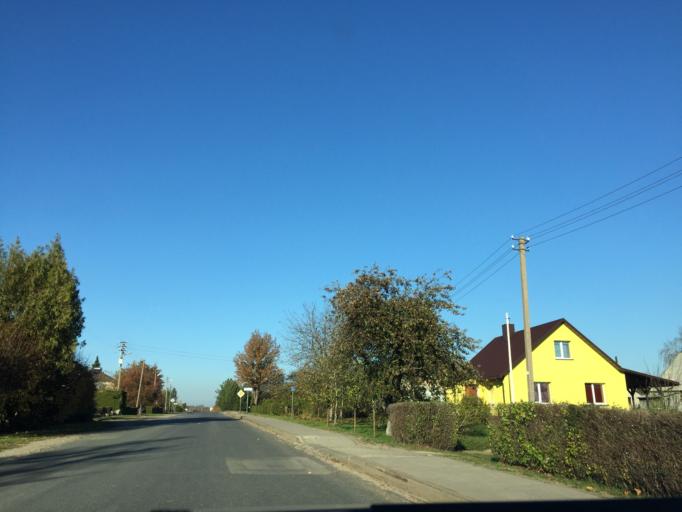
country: LT
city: Plateliai
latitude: 56.0456
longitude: 21.8176
